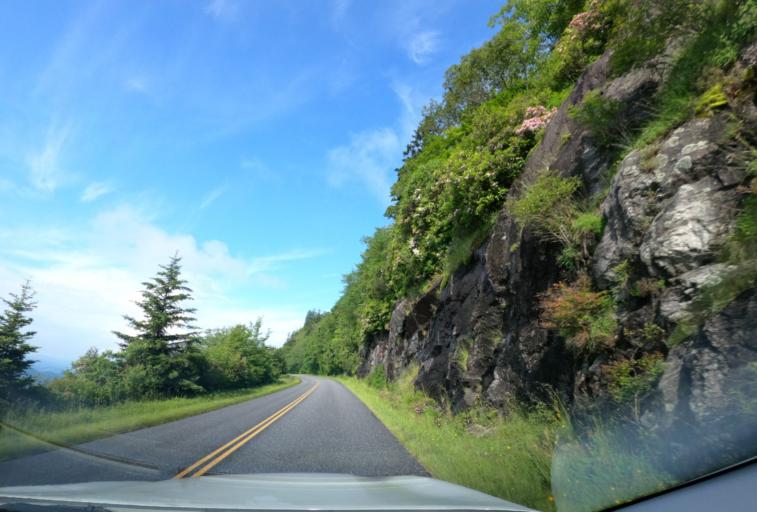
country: US
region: North Carolina
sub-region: Haywood County
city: Hazelwood
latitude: 35.3022
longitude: -82.9374
